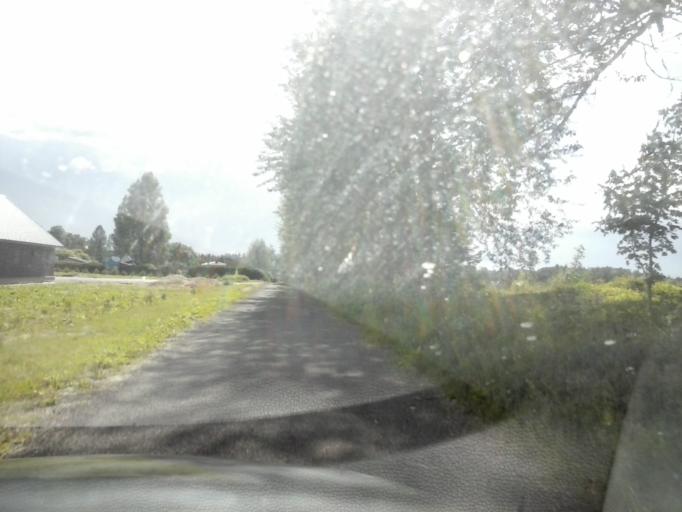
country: EE
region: Jaervamaa
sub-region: Koeru vald
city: Koeru
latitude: 58.9623
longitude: 26.0158
